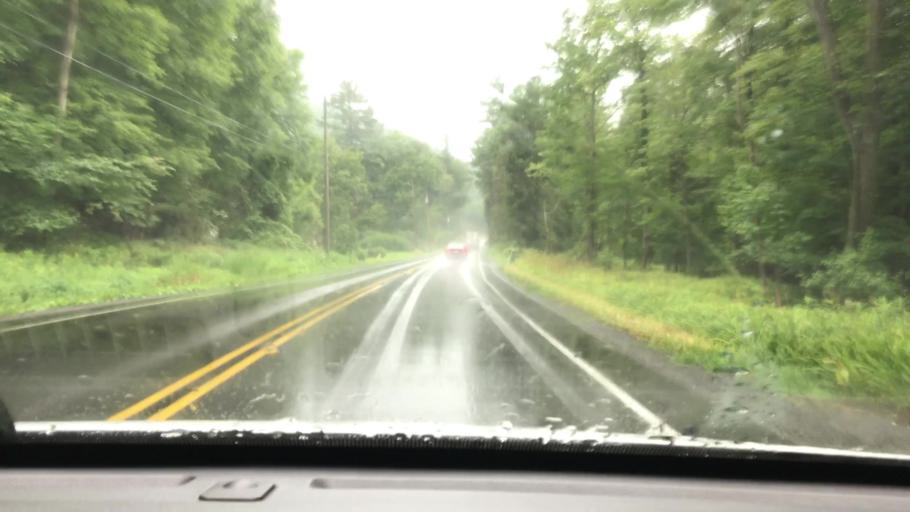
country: US
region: Pennsylvania
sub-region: Blair County
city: Tyrone
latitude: 40.7485
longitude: -78.2120
